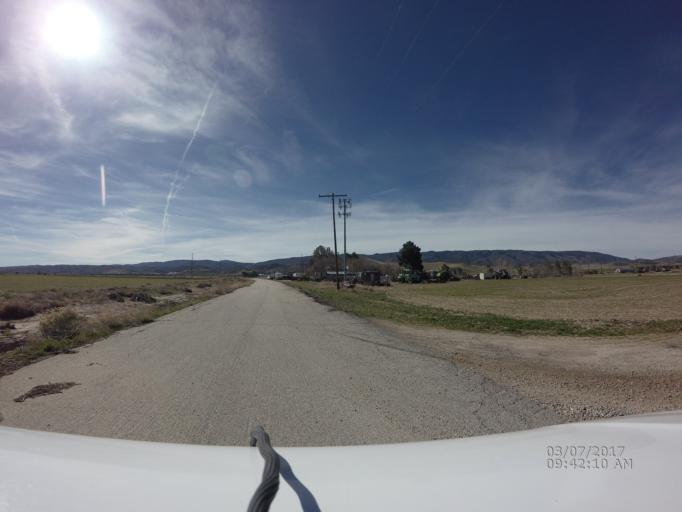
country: US
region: California
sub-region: Los Angeles County
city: Green Valley
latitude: 34.7849
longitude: -118.6077
